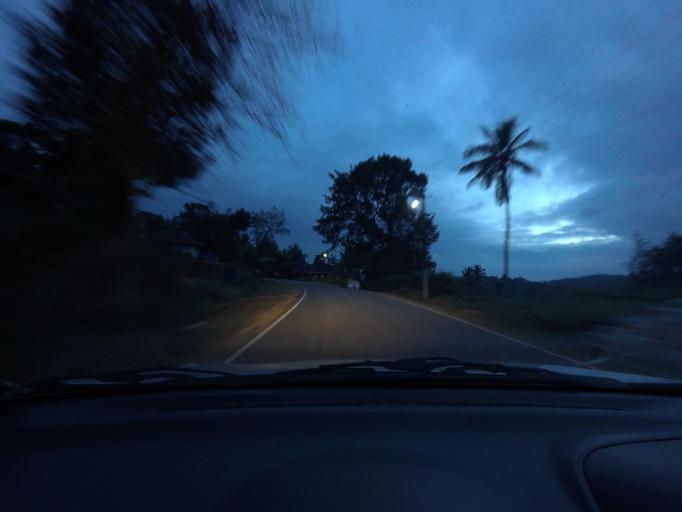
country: IN
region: Karnataka
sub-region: Hassan
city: Sakleshpur
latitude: 12.9999
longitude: 75.6978
